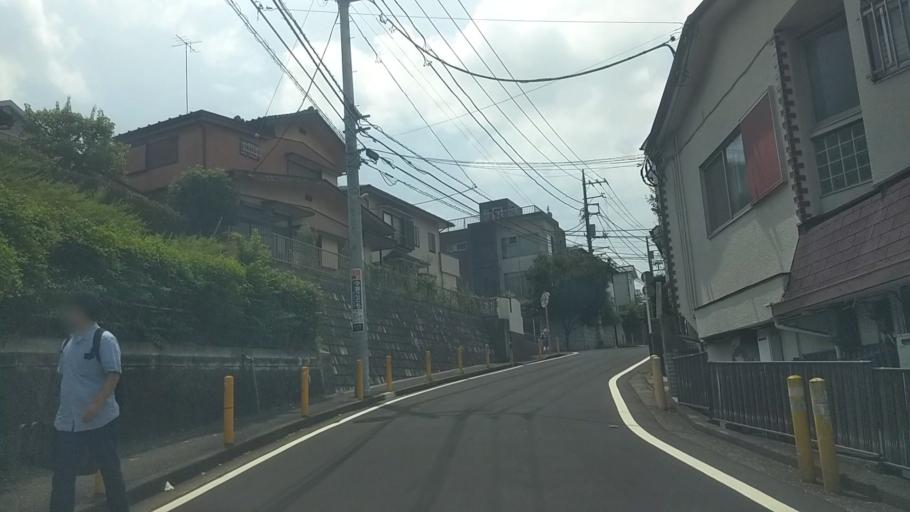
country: JP
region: Kanagawa
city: Yokohama
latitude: 35.5090
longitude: 139.6307
